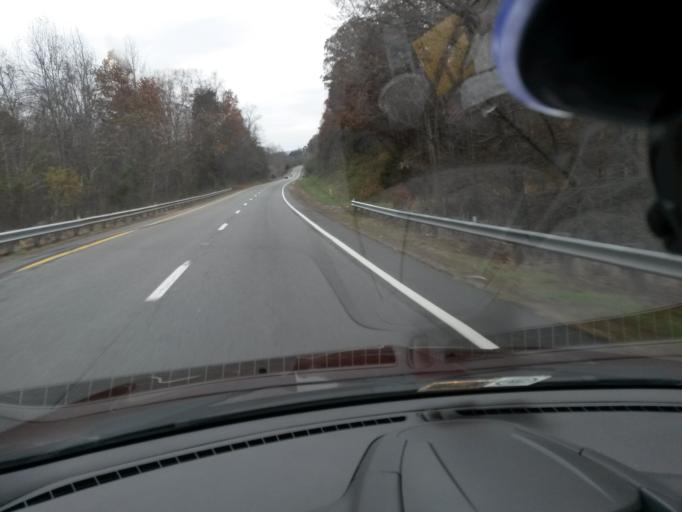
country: US
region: Virginia
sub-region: Nelson County
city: Nellysford
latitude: 37.8436
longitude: -78.7775
